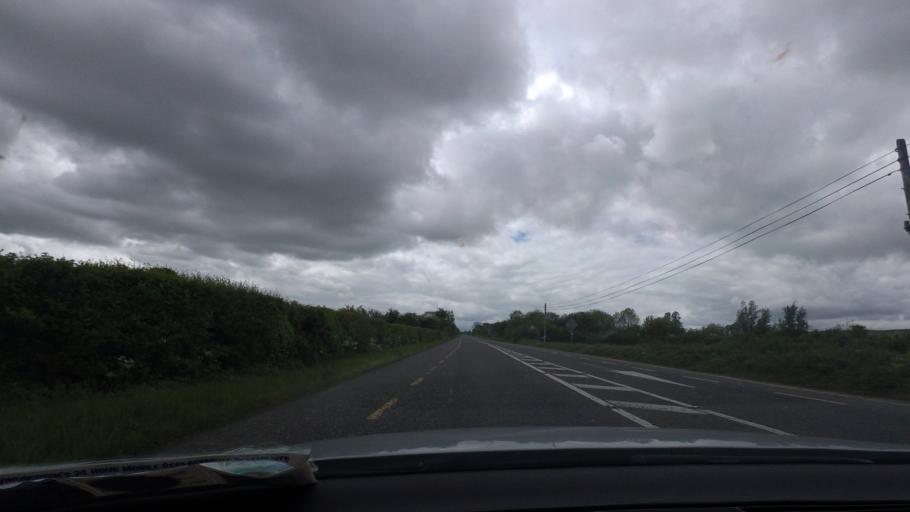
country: IE
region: Munster
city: Thurles
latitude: 52.6093
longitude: -7.7848
